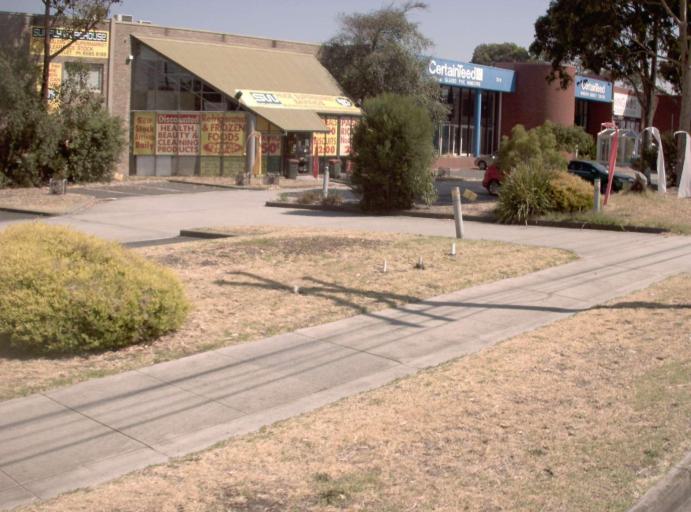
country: AU
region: Victoria
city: Heatherton
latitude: -37.9559
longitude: 145.0762
